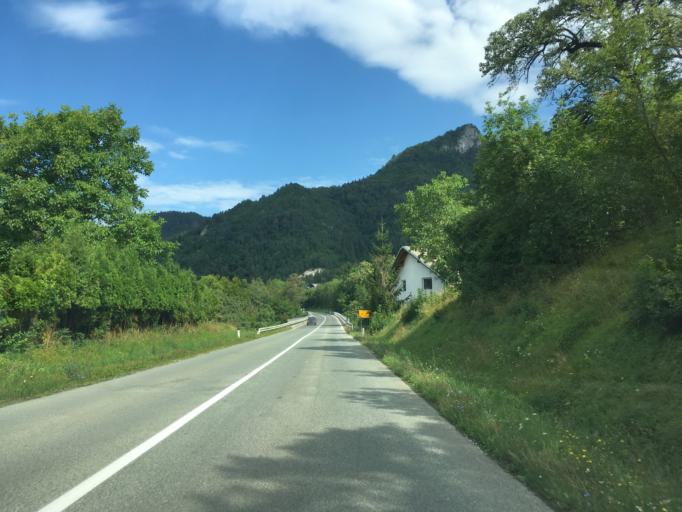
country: SI
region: Zirovnica
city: Zirovnica
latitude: 46.4078
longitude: 14.1311
